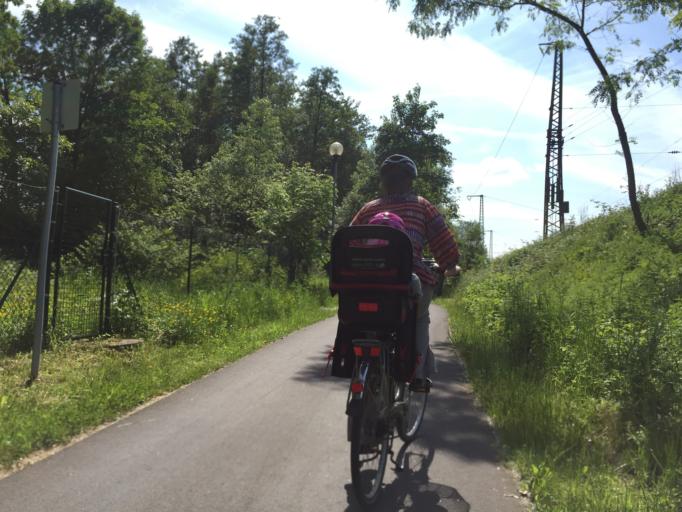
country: DE
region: Bavaria
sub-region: Regierungsbezirk Unterfranken
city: Goldbach
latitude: 49.9887
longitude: 9.1762
